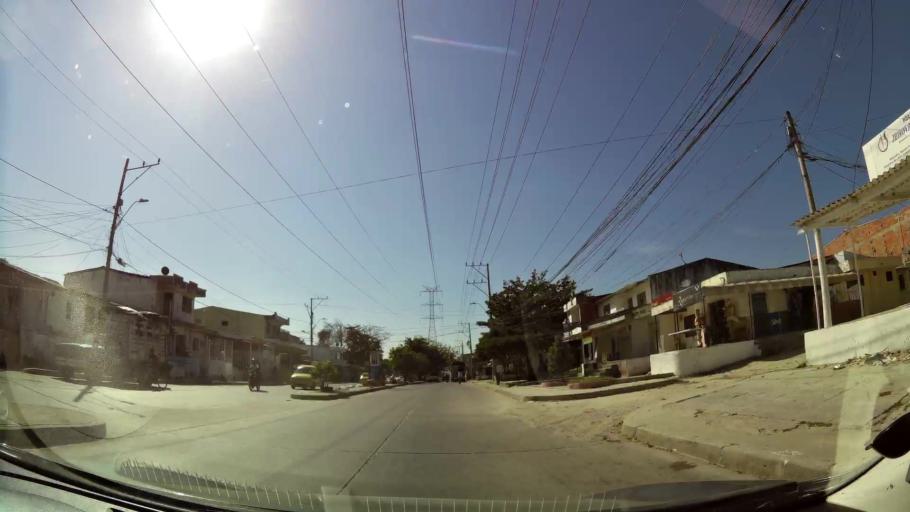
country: CO
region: Atlantico
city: Soledad
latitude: 10.9296
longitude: -74.7943
